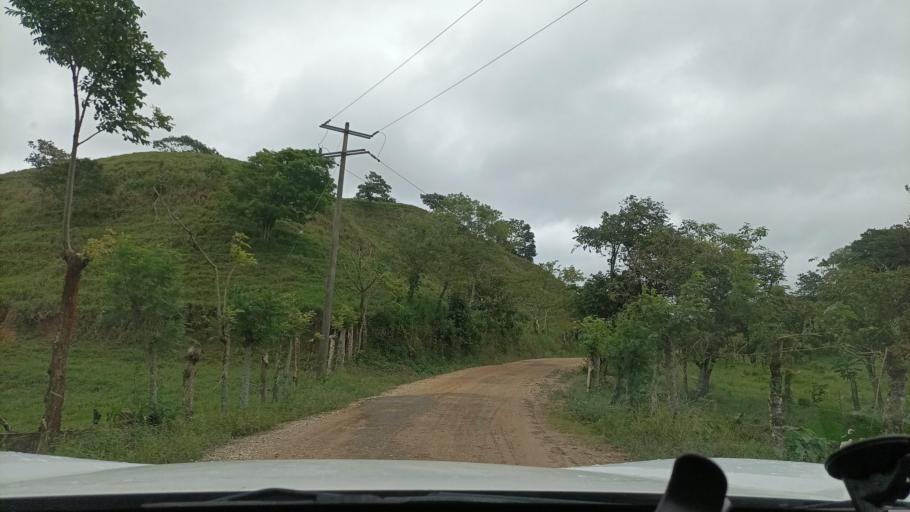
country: MX
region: Veracruz
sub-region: Moloacan
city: Cuichapa
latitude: 17.7890
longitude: -94.3855
